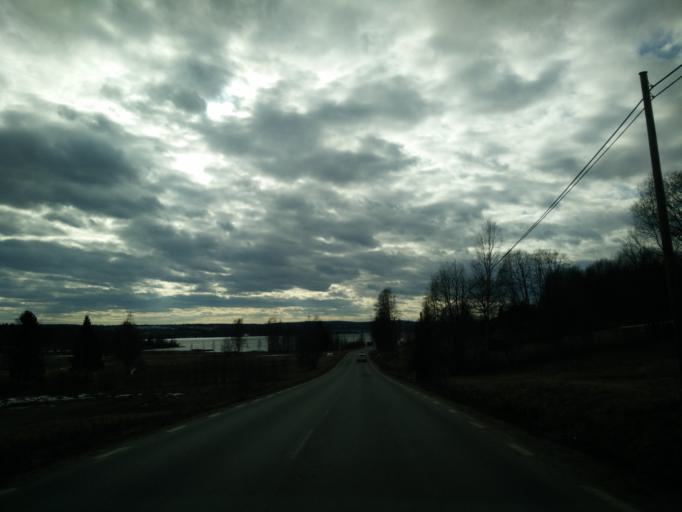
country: SE
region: Vaesternorrland
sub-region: Haernoesands Kommun
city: Haernoesand
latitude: 62.6723
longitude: 17.9533
